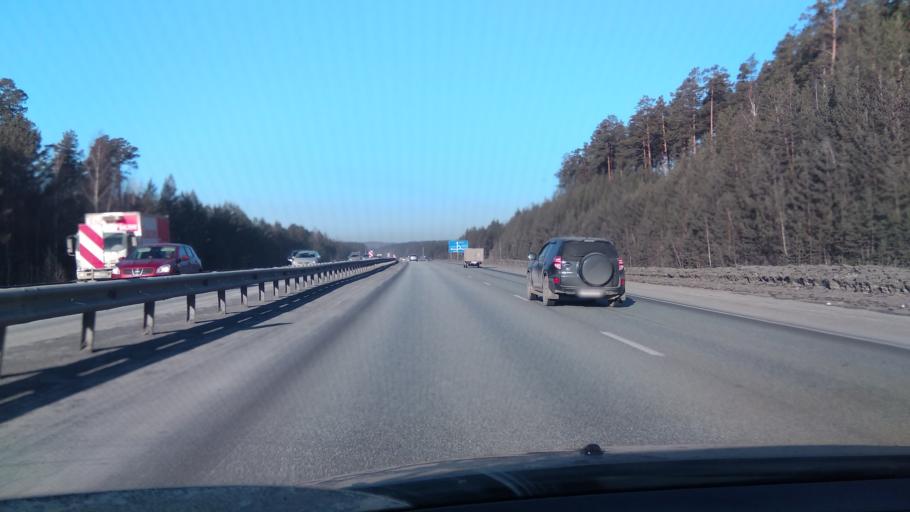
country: RU
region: Sverdlovsk
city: Severka
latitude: 56.8421
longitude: 60.2510
